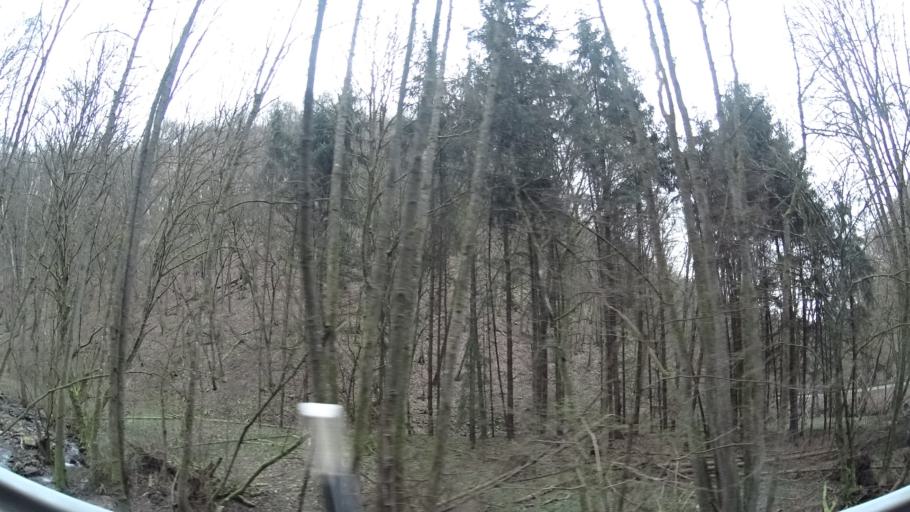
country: DE
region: Rheinland-Pfalz
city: Langenthal
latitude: 49.8428
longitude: 7.5670
